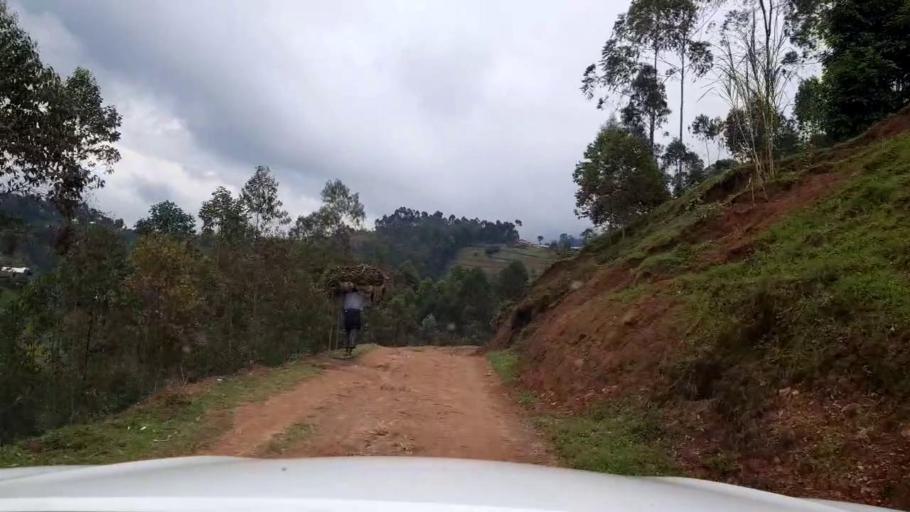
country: RW
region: Northern Province
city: Musanze
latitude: -1.5964
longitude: 29.7799
